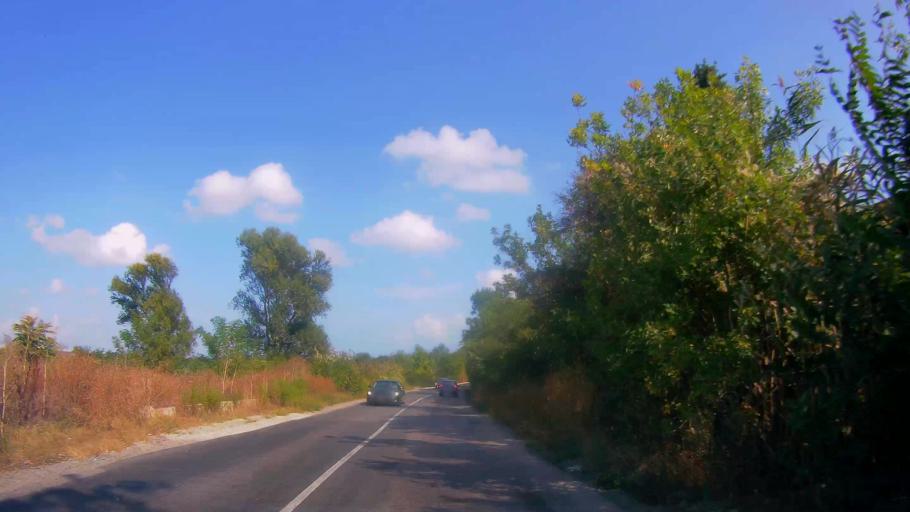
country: BG
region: Burgas
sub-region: Obshtina Burgas
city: Burgas
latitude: 42.4732
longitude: 27.4233
